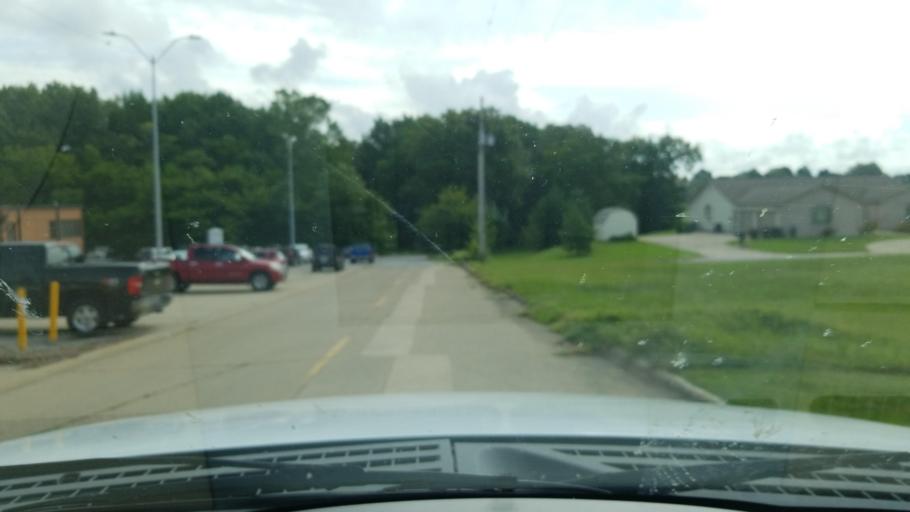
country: US
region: Illinois
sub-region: Saline County
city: Harrisburg
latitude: 37.7303
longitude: -88.5229
